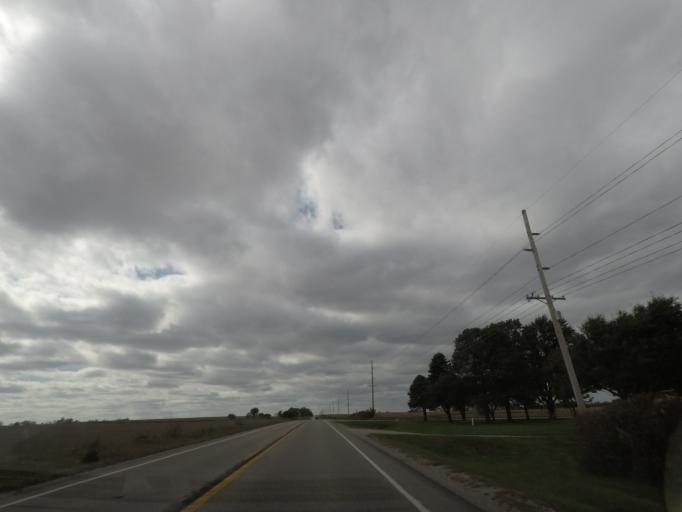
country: US
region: Iowa
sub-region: Story County
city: Huxley
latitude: 41.8778
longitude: -93.5401
